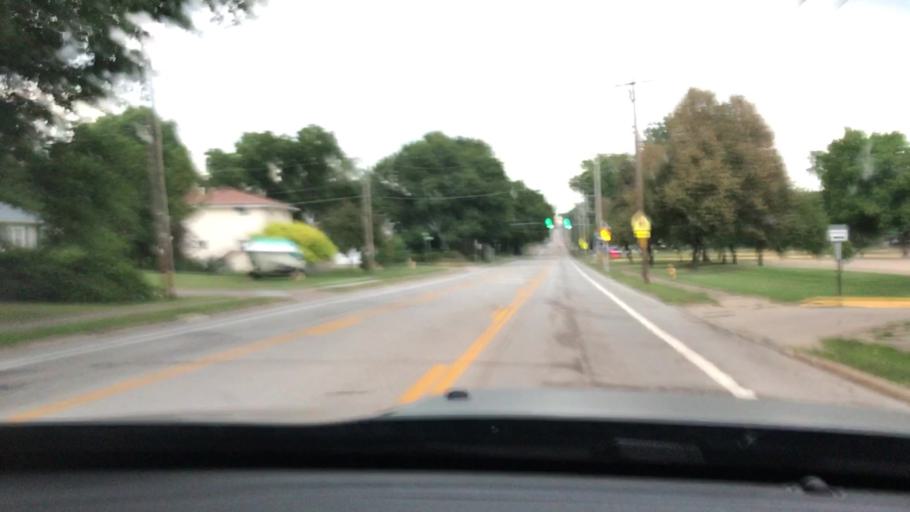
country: US
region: Iowa
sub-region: Scott County
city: Bettendorf
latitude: 41.5475
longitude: -90.5417
